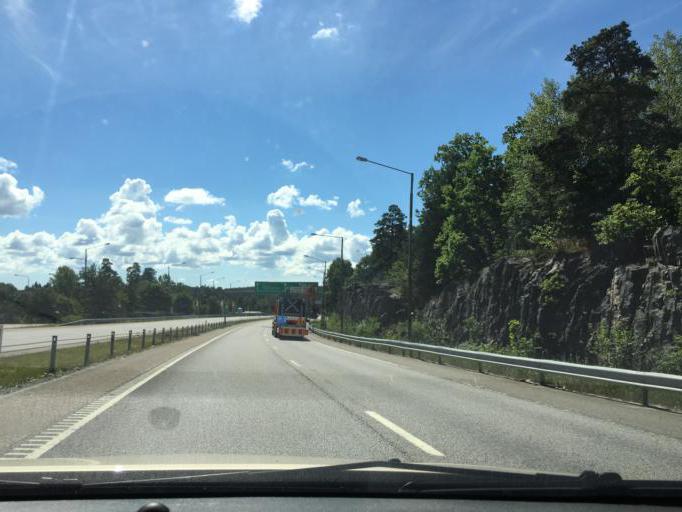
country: SE
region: Stockholm
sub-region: Nacka Kommun
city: Nacka
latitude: 59.3112
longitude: 18.1788
